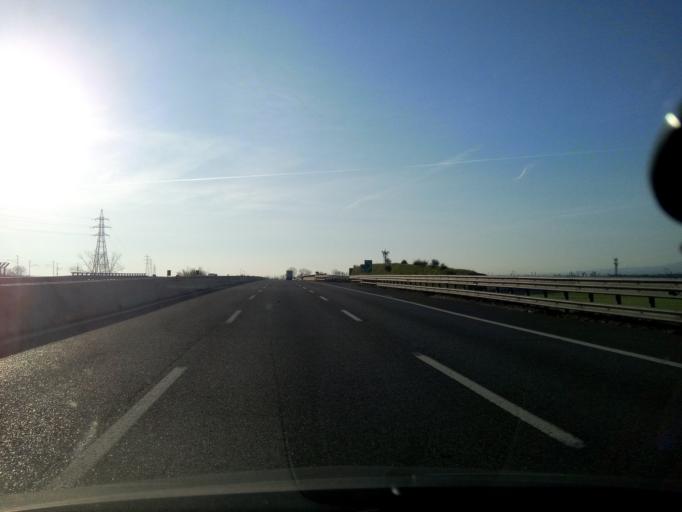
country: IT
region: Emilia-Romagna
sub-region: Provincia di Parma
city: Fidenza
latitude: 44.8994
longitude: 10.0418
